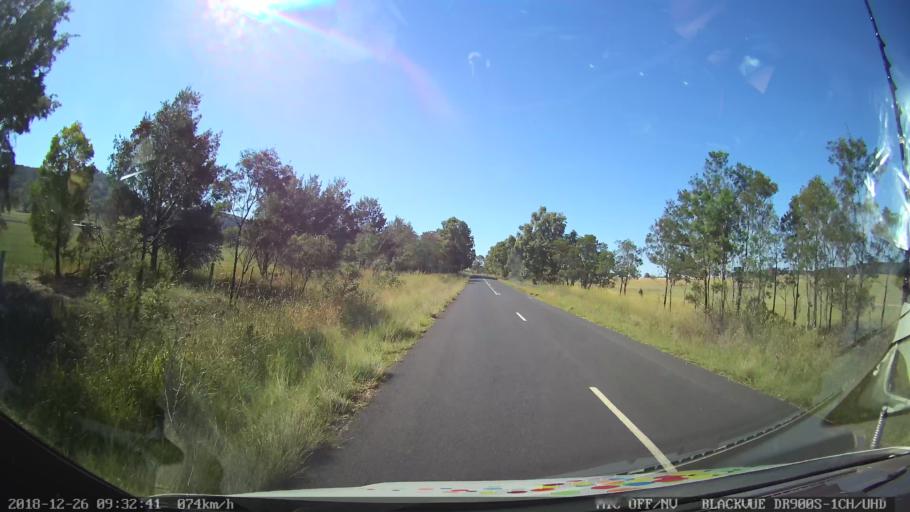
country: AU
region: New South Wales
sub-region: Mid-Western Regional
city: Kandos
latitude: -32.8870
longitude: 150.0328
